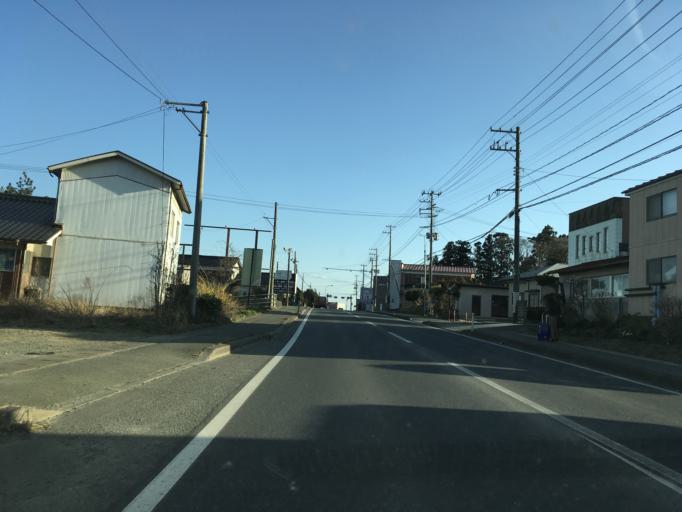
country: JP
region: Iwate
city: Ofunato
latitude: 38.8632
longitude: 141.5800
